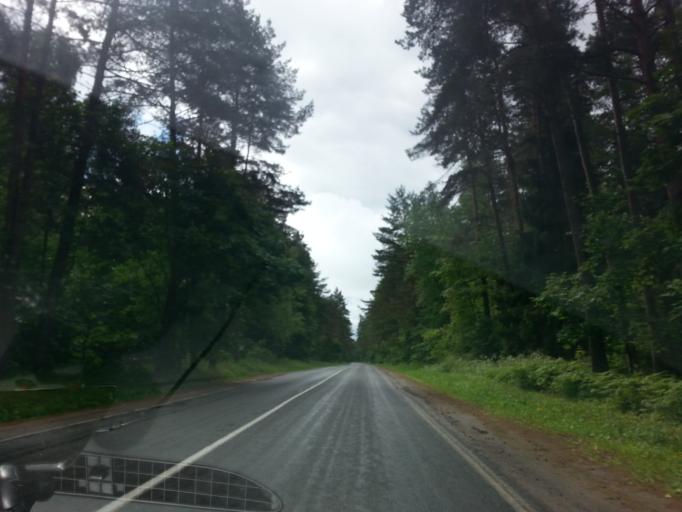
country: BY
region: Minsk
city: Narach
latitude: 54.9279
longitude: 26.7035
